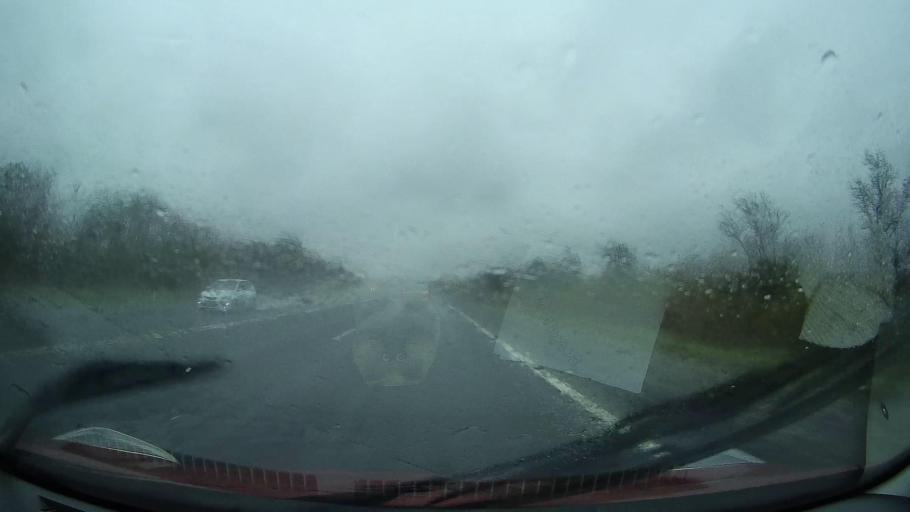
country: RU
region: Stavropol'skiy
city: Nevinnomyssk
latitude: 44.6193
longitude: 42.0945
